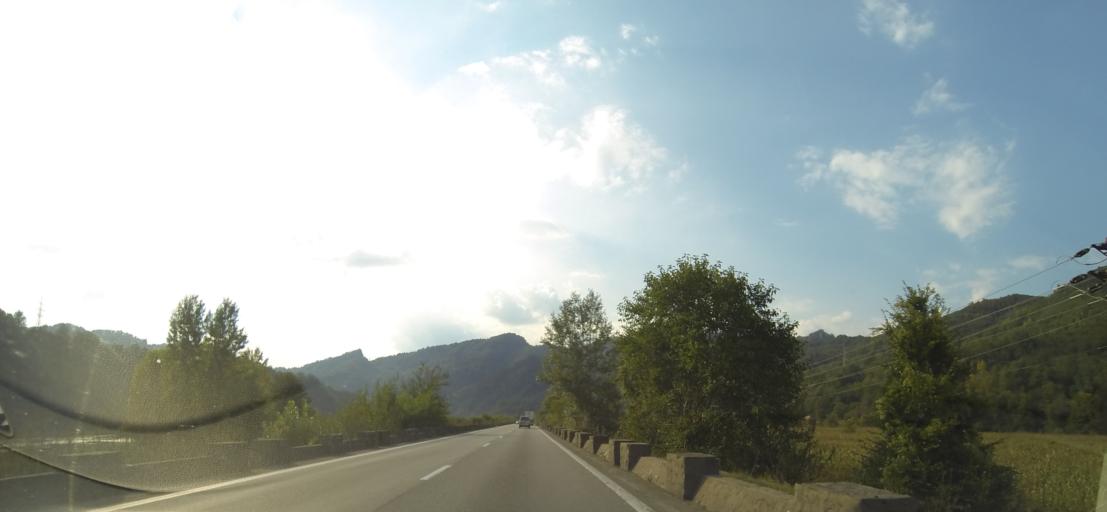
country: RO
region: Valcea
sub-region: Comuna Brezoi
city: Brezoi
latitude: 45.3525
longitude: 24.2830
